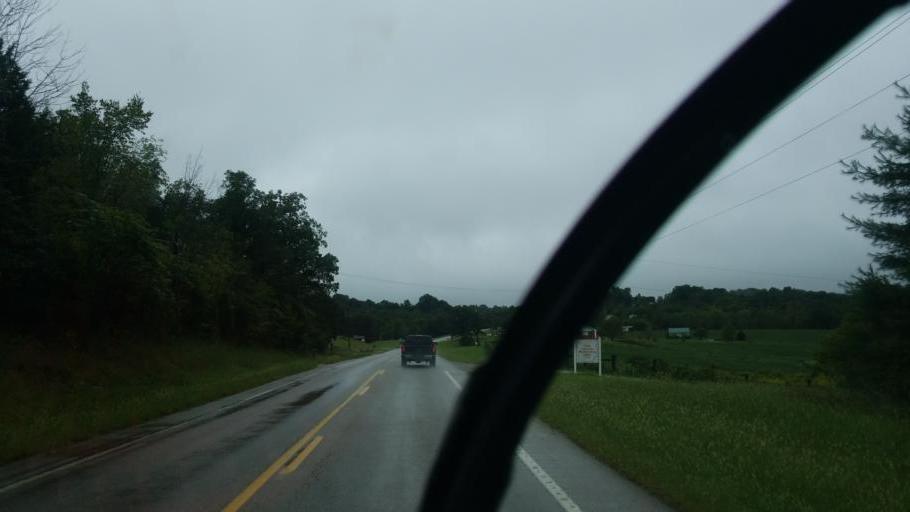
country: US
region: Ohio
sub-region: Adams County
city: West Union
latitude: 38.7964
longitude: -83.5113
